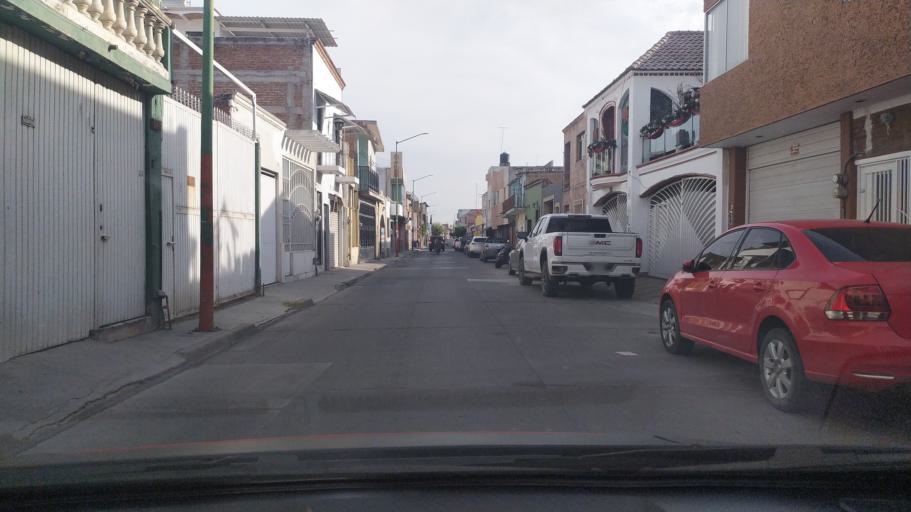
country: MX
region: Guanajuato
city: San Francisco del Rincon
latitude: 21.0194
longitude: -101.8542
